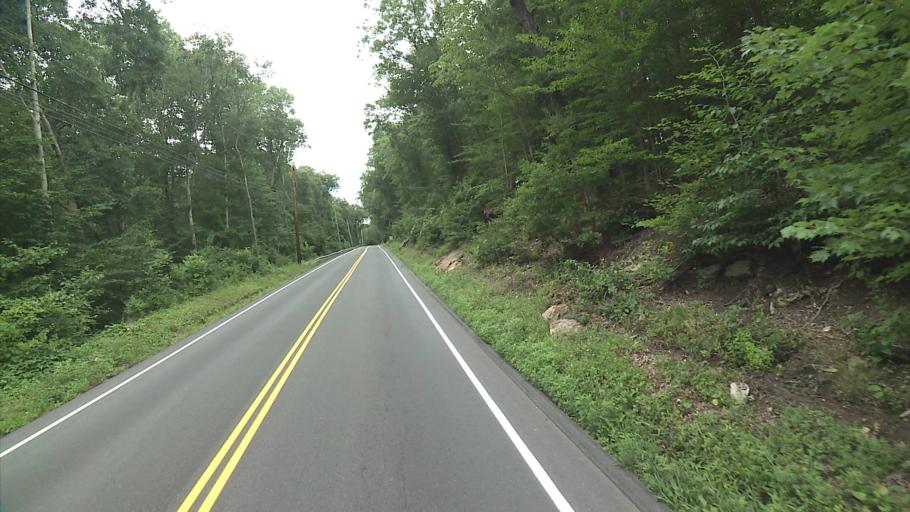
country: US
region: Connecticut
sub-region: New Haven County
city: Heritage Village
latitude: 41.5139
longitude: -73.2538
